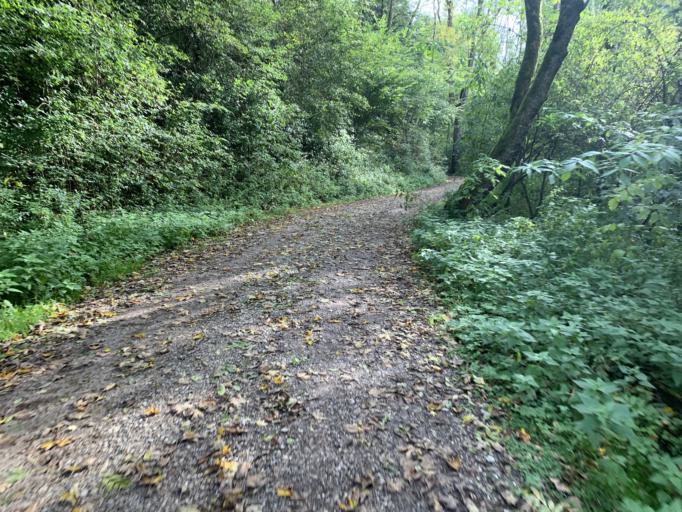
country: DE
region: Bavaria
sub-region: Upper Bavaria
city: Grunwald
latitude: 48.0302
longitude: 11.5095
